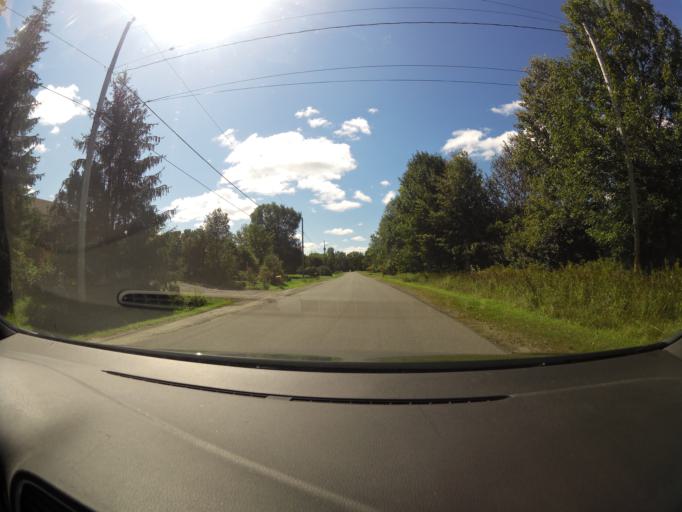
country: CA
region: Ontario
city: Carleton Place
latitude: 45.2407
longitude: -76.1647
